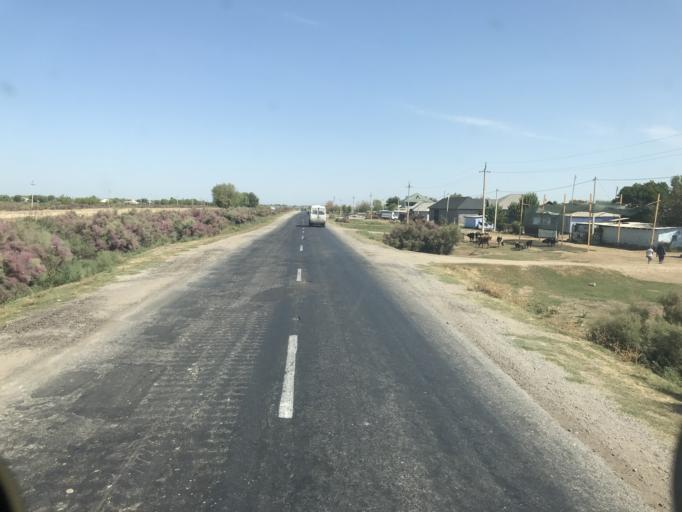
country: KZ
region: Ongtustik Qazaqstan
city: Myrzakent
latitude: 40.7300
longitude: 68.5365
